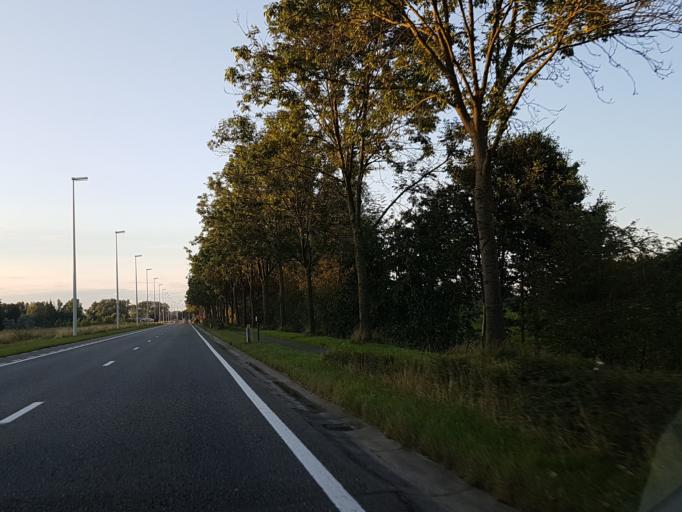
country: BE
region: Flanders
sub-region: Provincie Oost-Vlaanderen
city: Hamme
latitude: 51.0637
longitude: 4.1235
